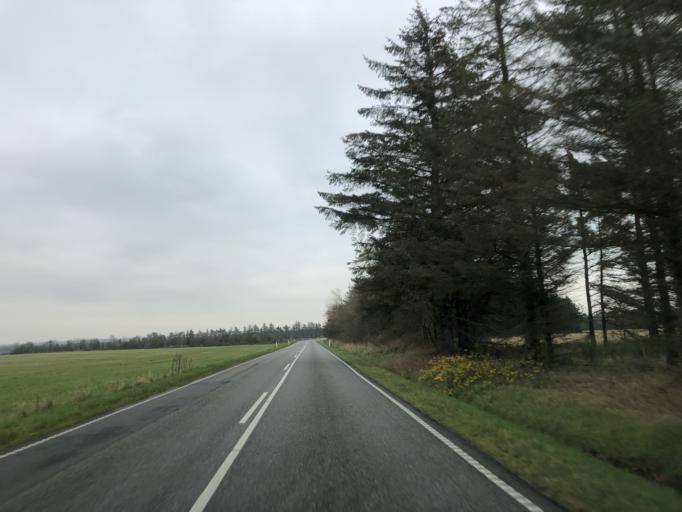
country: DK
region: Central Jutland
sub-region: Holstebro Kommune
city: Ulfborg
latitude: 56.1964
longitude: 8.3598
